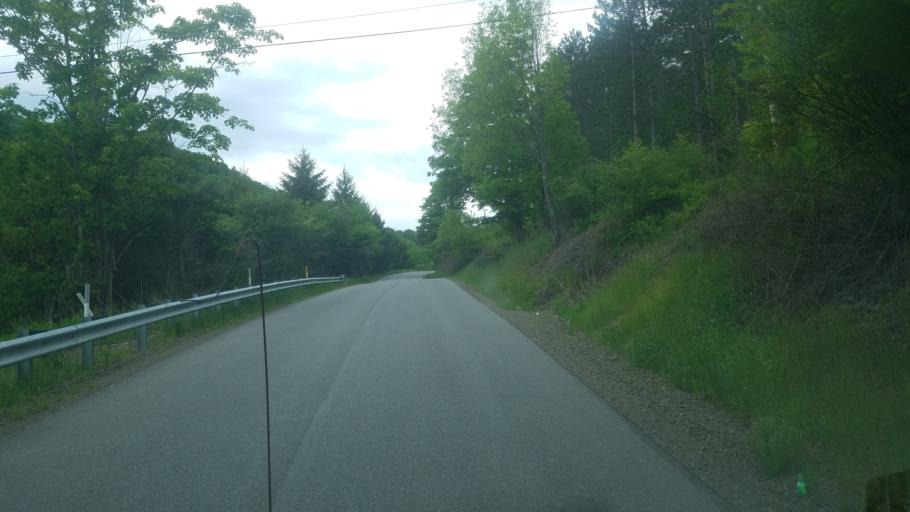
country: US
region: Pennsylvania
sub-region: Tioga County
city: Westfield
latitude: 41.8218
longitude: -77.5787
